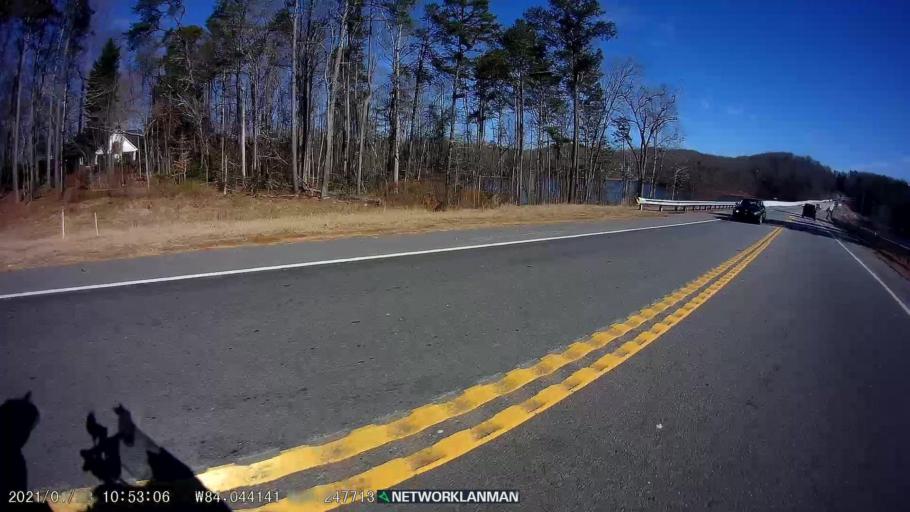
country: US
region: Georgia
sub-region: Forsyth County
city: Cumming
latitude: 34.2476
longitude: -84.0440
